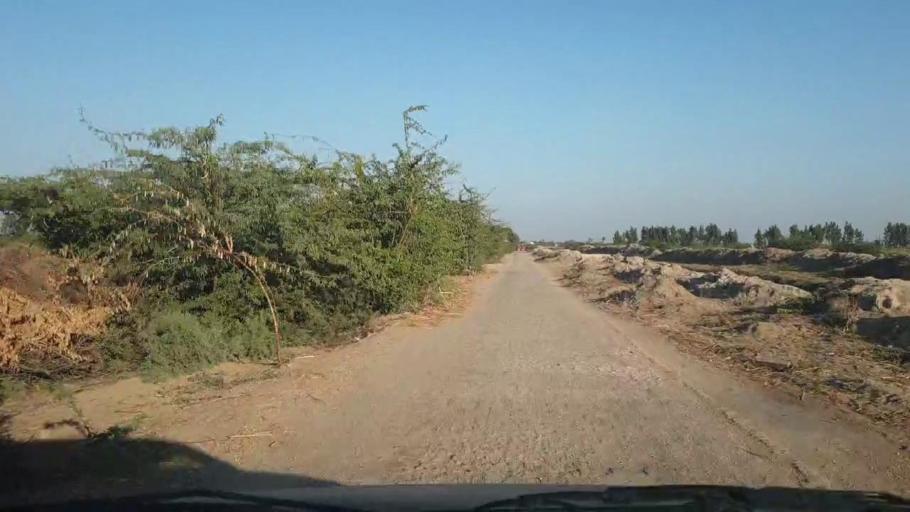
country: PK
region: Sindh
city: Samaro
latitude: 25.3188
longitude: 69.3022
